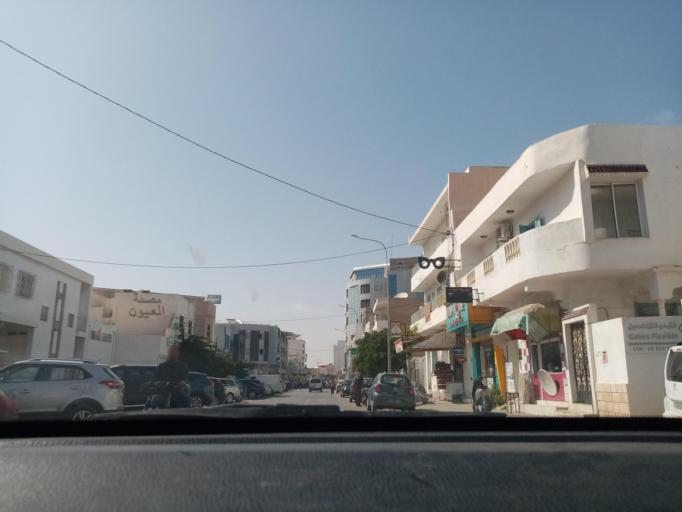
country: TN
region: Qabis
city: Gabes
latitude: 33.8854
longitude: 10.1050
